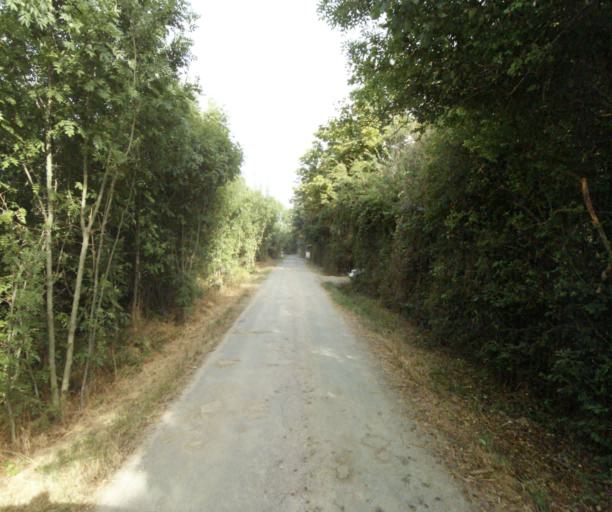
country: FR
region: Midi-Pyrenees
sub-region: Departement du Tarn
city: Puylaurens
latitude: 43.5358
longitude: 2.0452
